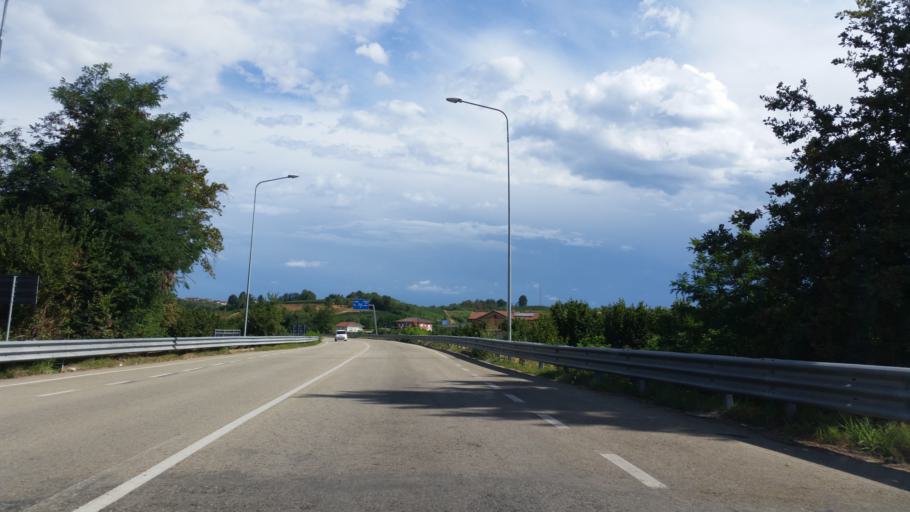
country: IT
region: Piedmont
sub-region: Provincia di Cuneo
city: Monta
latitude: 44.8174
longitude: 7.9477
